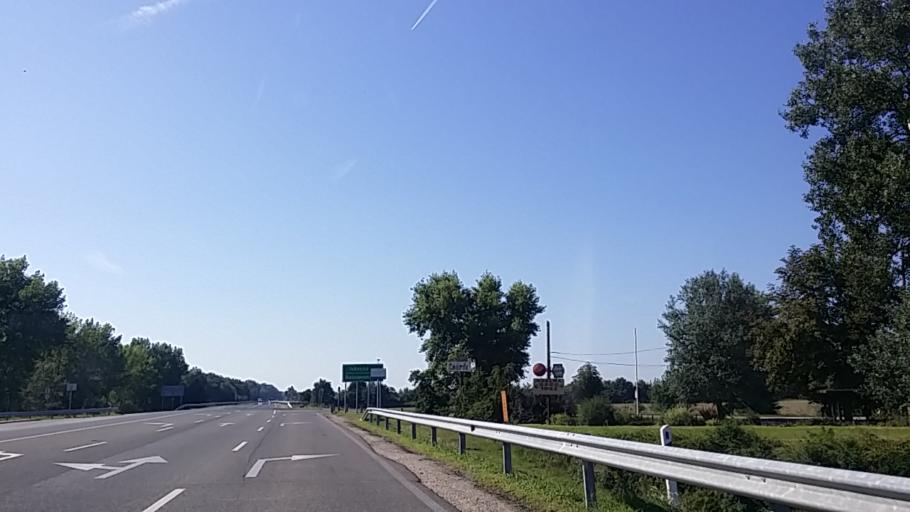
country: HU
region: Fejer
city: Adony
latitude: 47.1414
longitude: 18.8610
